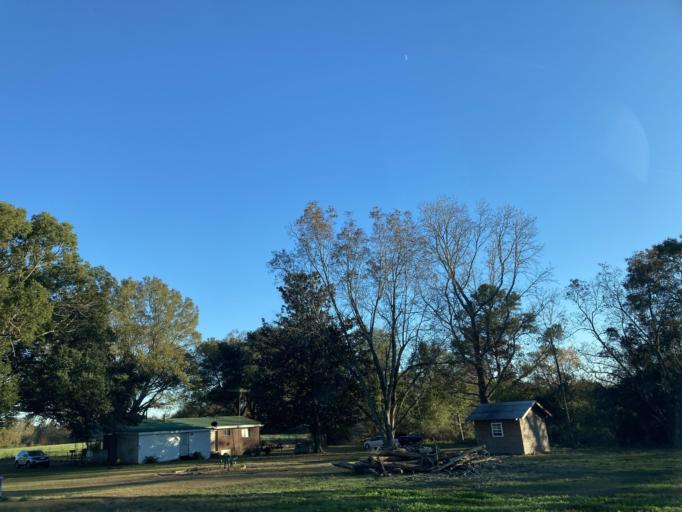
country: US
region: Mississippi
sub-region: Lamar County
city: Sumrall
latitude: 31.2672
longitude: -89.6039
